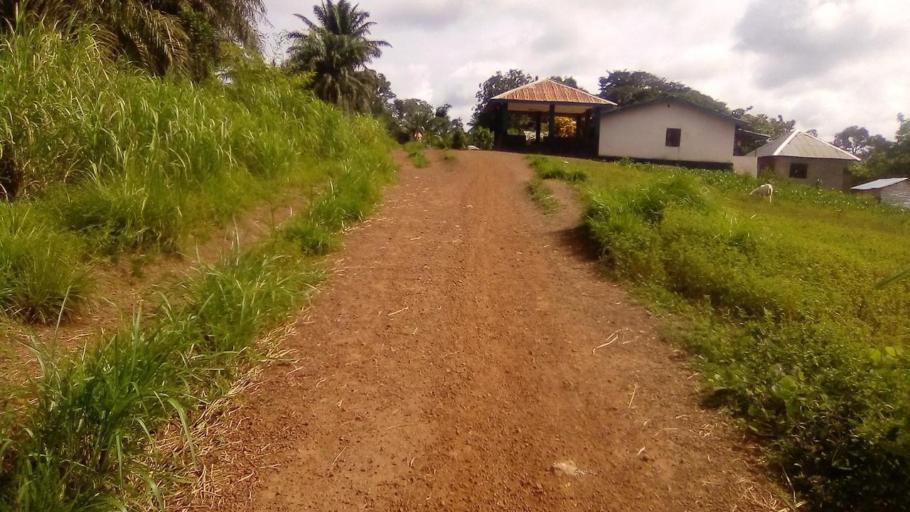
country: SL
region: Southern Province
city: Pujehun
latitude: 7.3732
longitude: -11.7281
